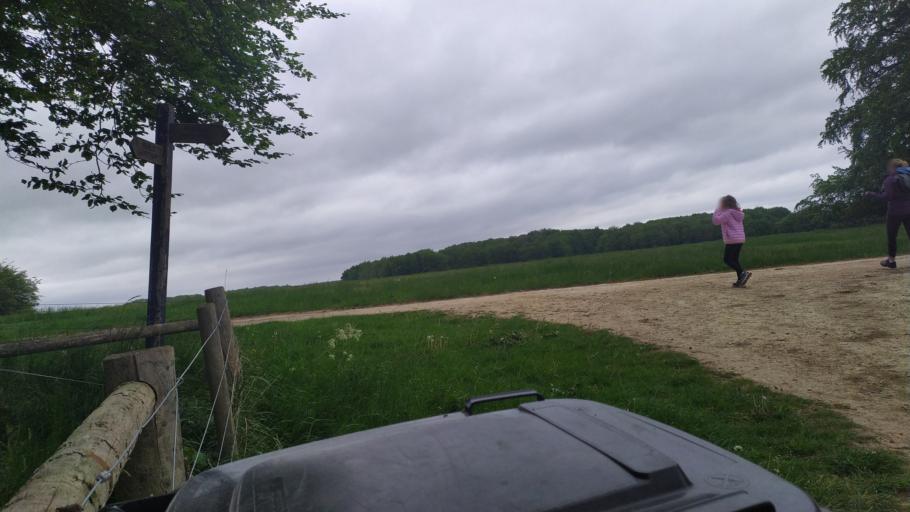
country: GB
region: England
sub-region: City and Borough of Leeds
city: Bramham
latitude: 53.8603
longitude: -1.3848
